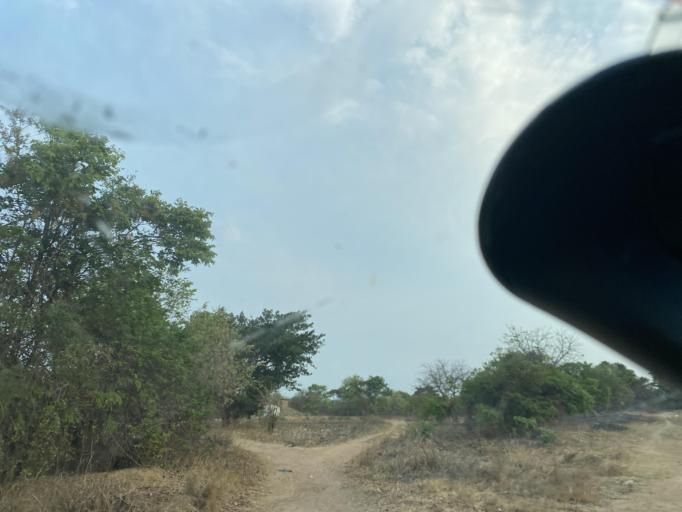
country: ZM
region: Lusaka
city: Chongwe
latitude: -15.2090
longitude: 28.5009
